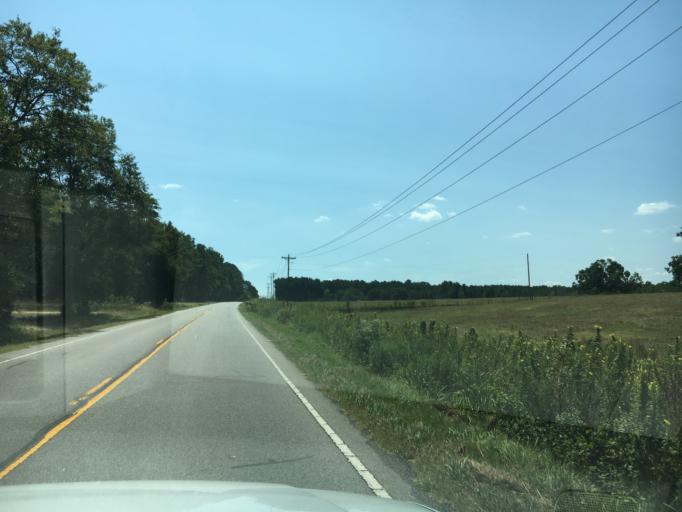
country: US
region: South Carolina
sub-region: Saluda County
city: Saluda
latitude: 33.9096
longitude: -81.7032
